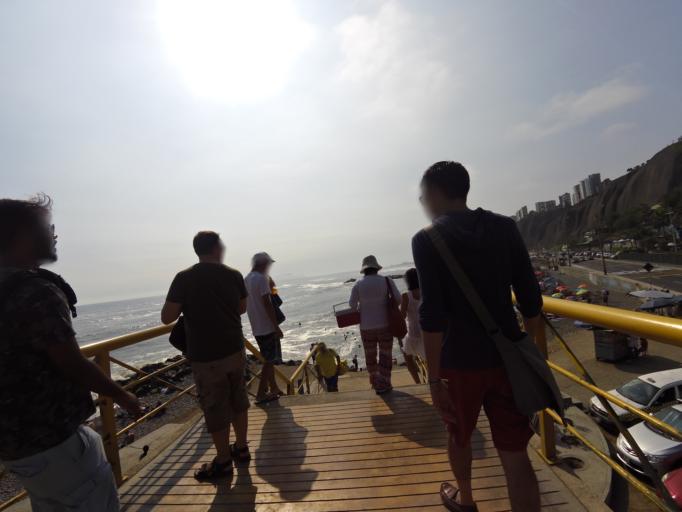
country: PE
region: Lima
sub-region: Lima
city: San Isidro
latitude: -12.1287
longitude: -77.0368
